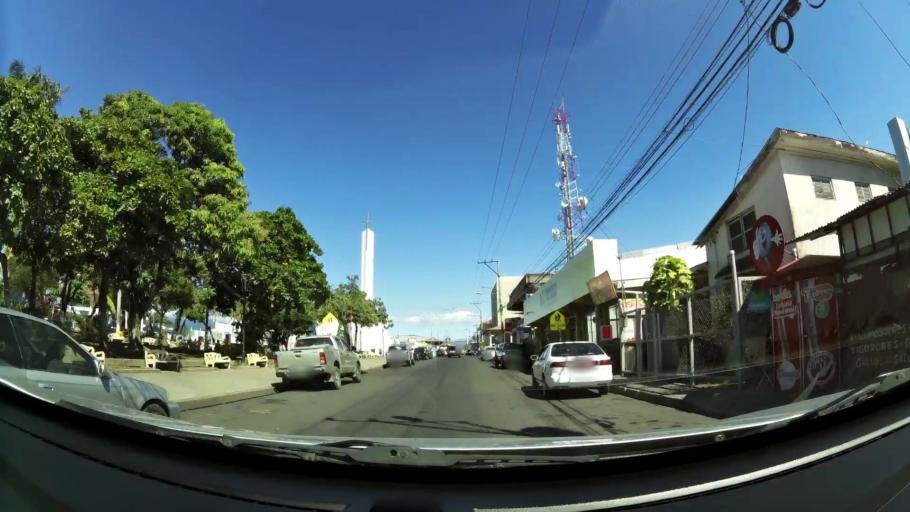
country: CR
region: Guanacaste
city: Liberia
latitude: 10.6293
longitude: -85.4383
